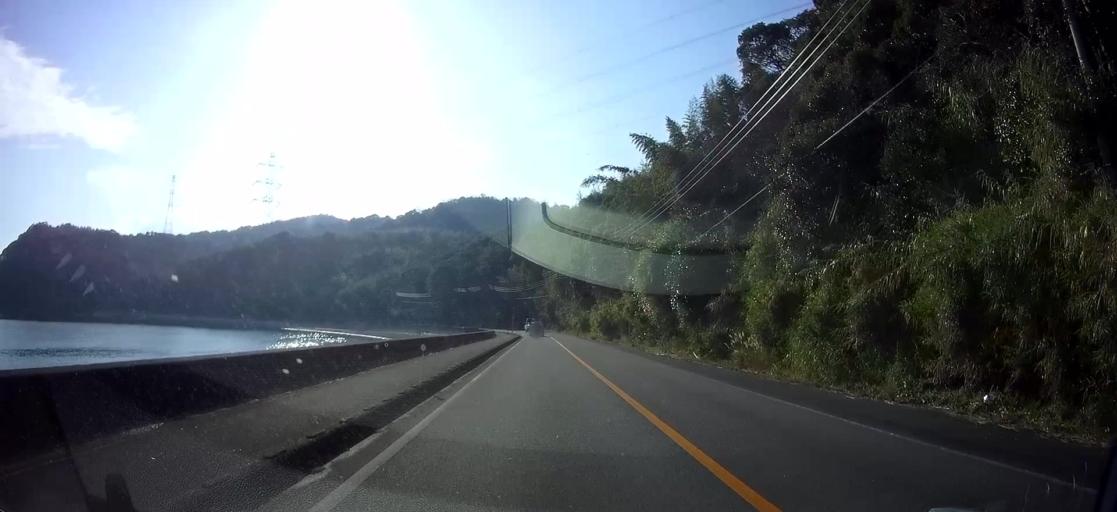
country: JP
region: Kumamoto
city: Yatsushiro
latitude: 32.5118
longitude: 130.4526
